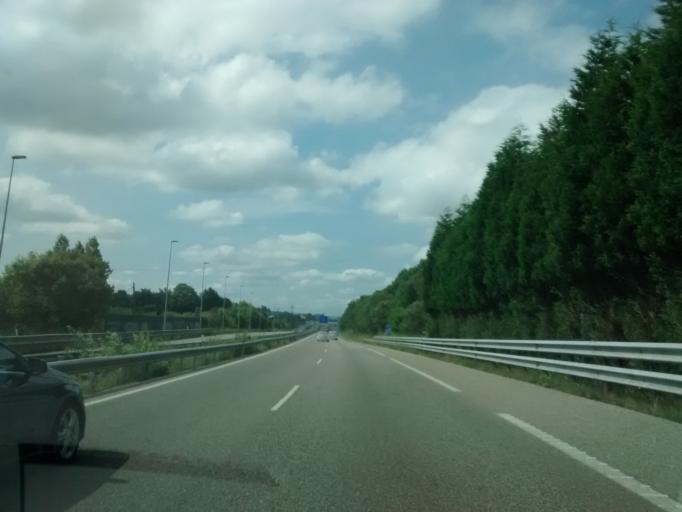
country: ES
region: Asturias
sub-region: Province of Asturias
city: Pola de Siero
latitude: 43.3722
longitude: -5.6821
